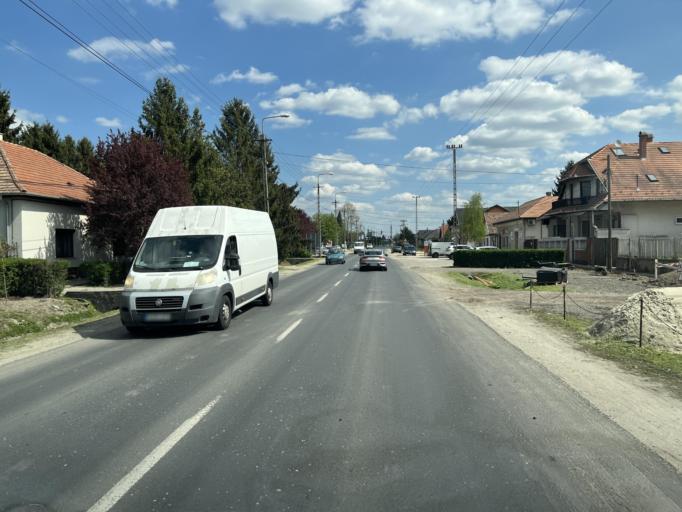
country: HU
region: Pest
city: Ullo
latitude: 47.3840
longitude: 19.3480
